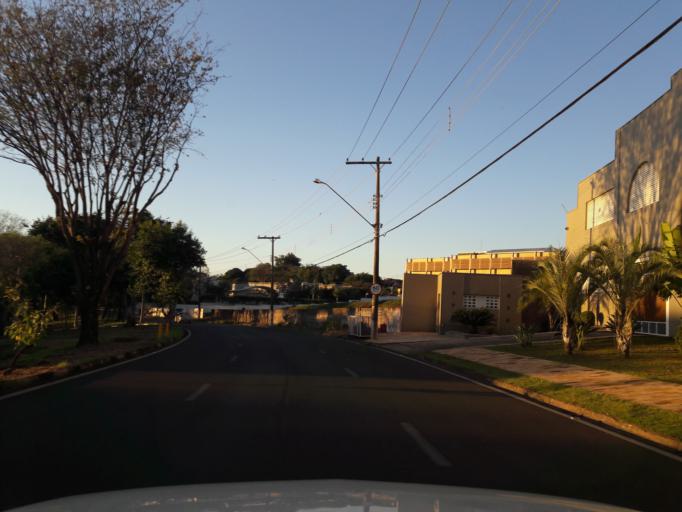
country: BR
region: Sao Paulo
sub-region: Moji-Guacu
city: Mogi-Gaucu
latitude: -22.3646
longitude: -46.9338
